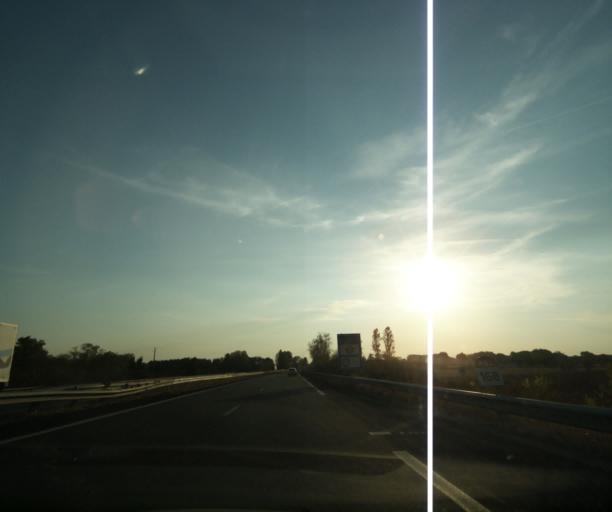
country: FR
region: Midi-Pyrenees
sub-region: Departement du Tarn-et-Garonne
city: Castelsarrasin
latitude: 44.0502
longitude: 1.0893
